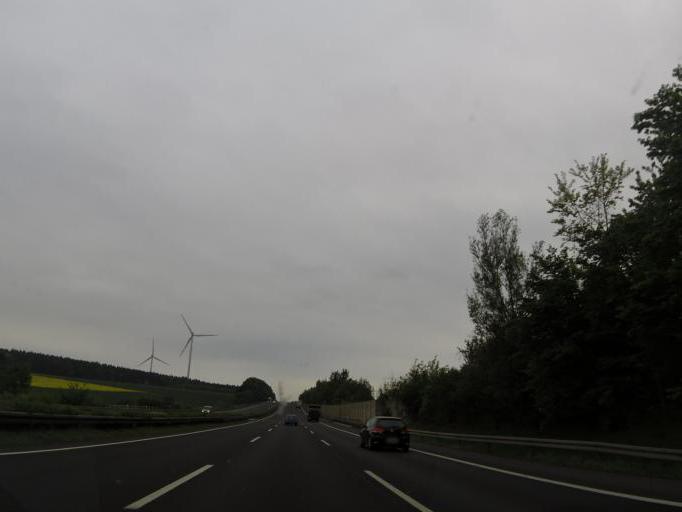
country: DE
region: Hesse
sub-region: Regierungsbezirk Kassel
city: Fuldatal
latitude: 51.3440
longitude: 9.5992
